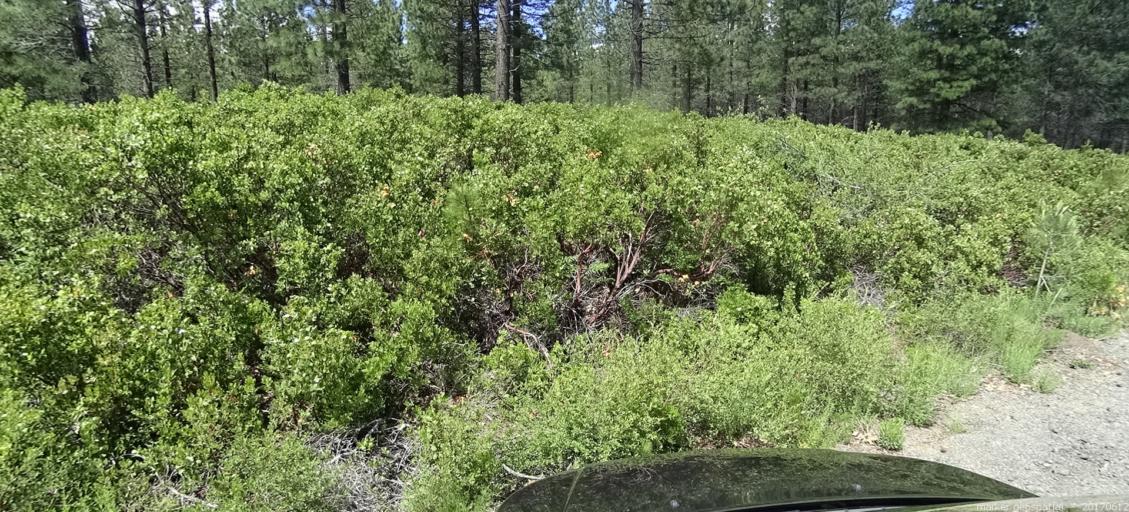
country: US
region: California
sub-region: Siskiyou County
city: Mount Shasta
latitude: 41.2987
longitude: -122.2872
